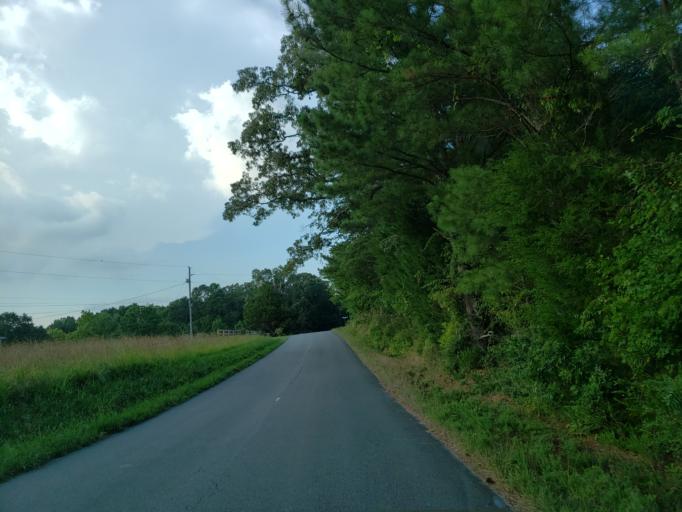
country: US
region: Georgia
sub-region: Bartow County
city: Euharlee
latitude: 34.0855
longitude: -84.9357
